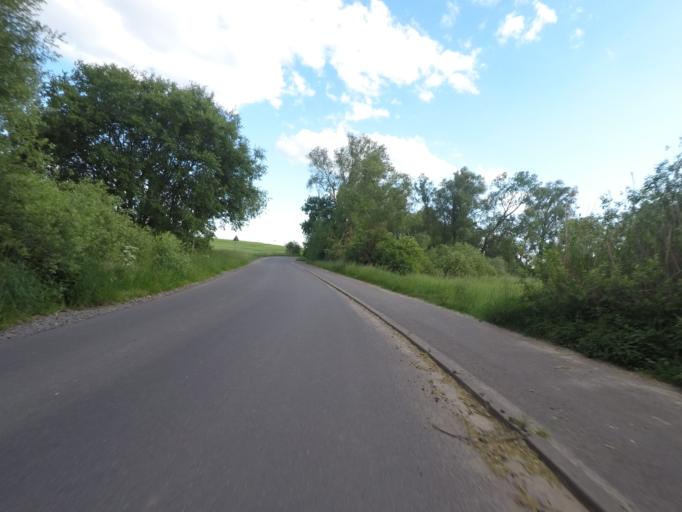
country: DE
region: Brandenburg
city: Britz
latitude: 52.8870
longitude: 13.7690
